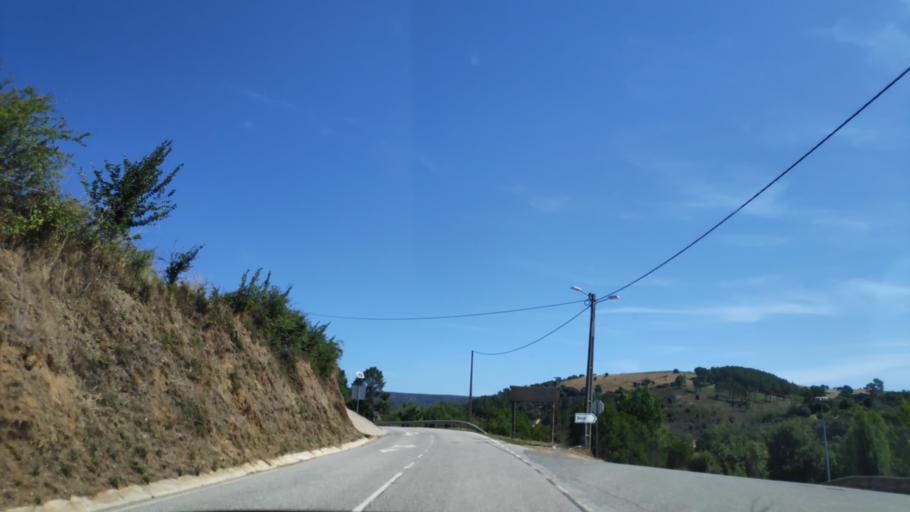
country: PT
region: Braganca
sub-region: Braganca Municipality
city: Braganca
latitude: 41.8719
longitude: -6.7490
